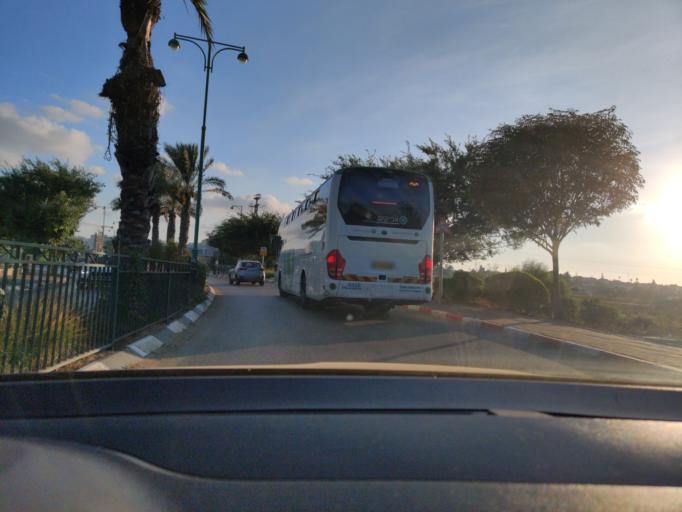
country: IL
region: Haifa
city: Hadera
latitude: 32.4431
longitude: 34.9346
